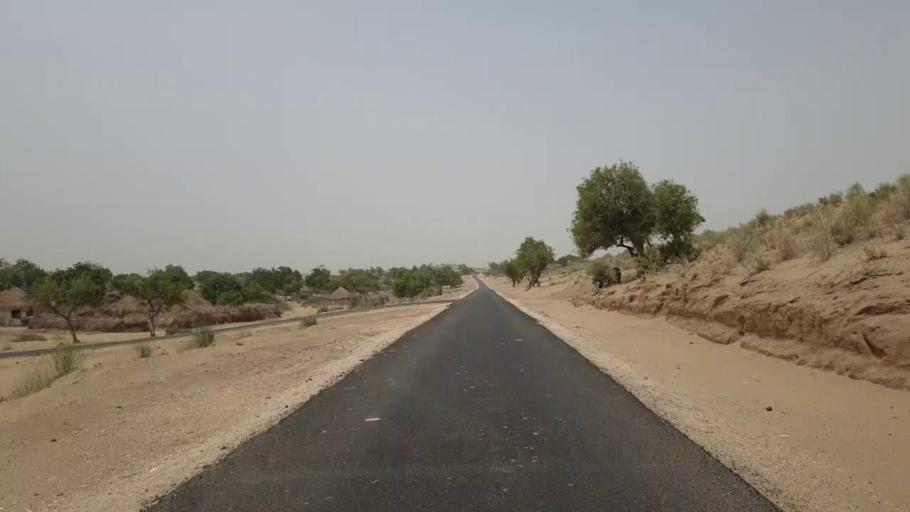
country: PK
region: Sindh
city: Islamkot
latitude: 24.8048
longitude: 70.5576
